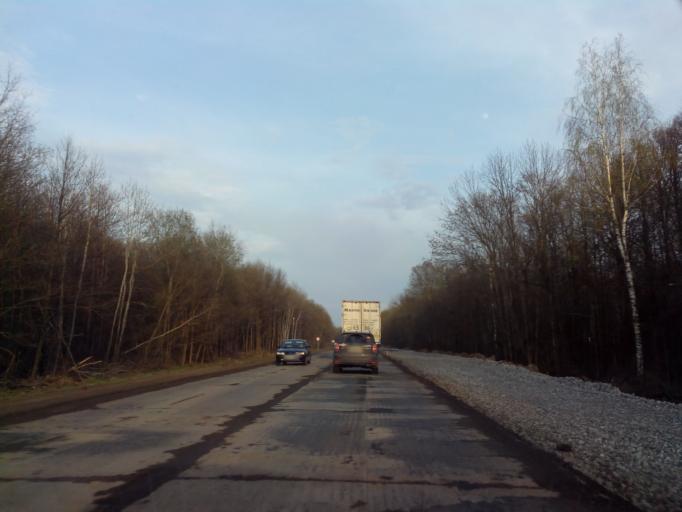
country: RU
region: Rjazan
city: Zarechnyy
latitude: 53.7542
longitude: 39.7933
